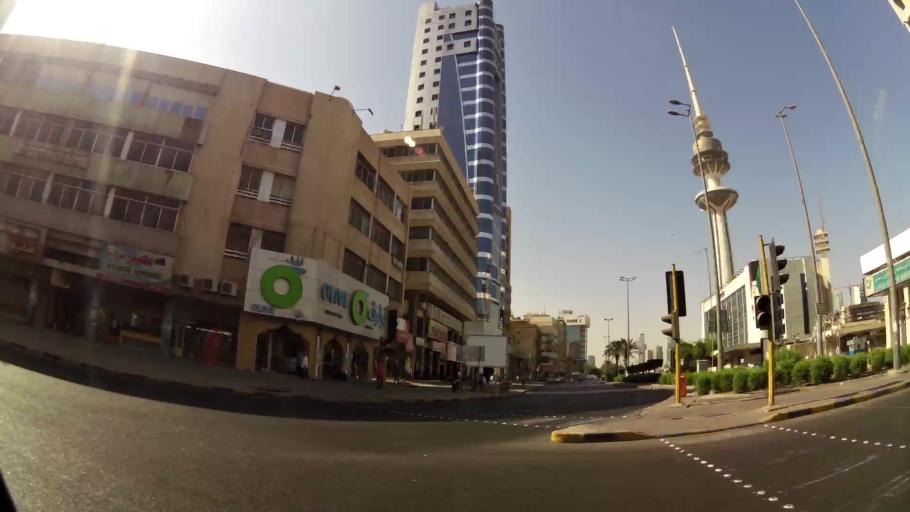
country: KW
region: Al Asimah
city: Kuwait City
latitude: 29.3693
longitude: 47.9789
